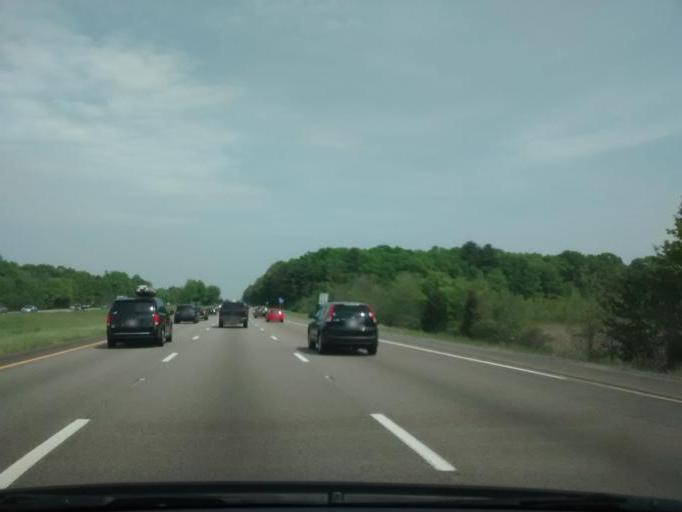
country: US
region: Massachusetts
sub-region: Bristol County
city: Mansfield Center
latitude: 41.9988
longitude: -71.2047
